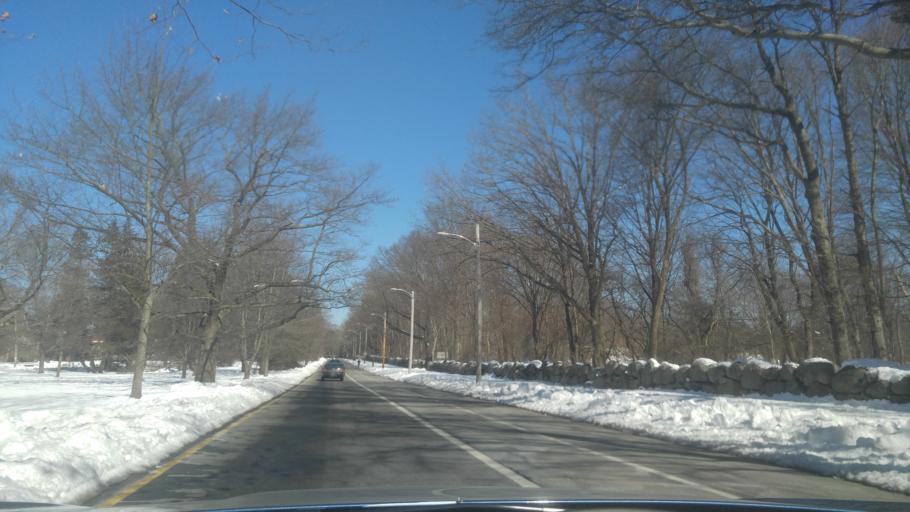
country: US
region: Rhode Island
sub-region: Providence County
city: Pawtucket
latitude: 41.8470
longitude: -71.3868
